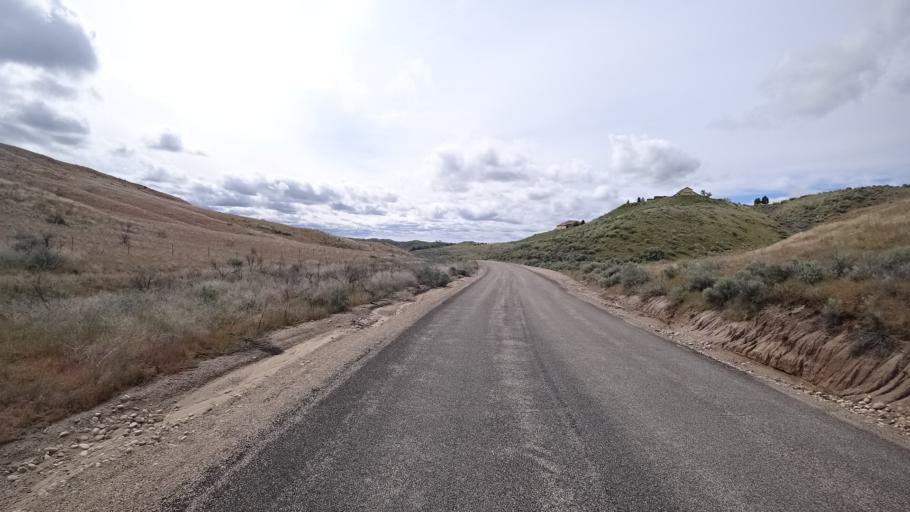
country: US
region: Idaho
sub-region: Ada County
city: Eagle
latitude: 43.7579
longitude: -116.3675
